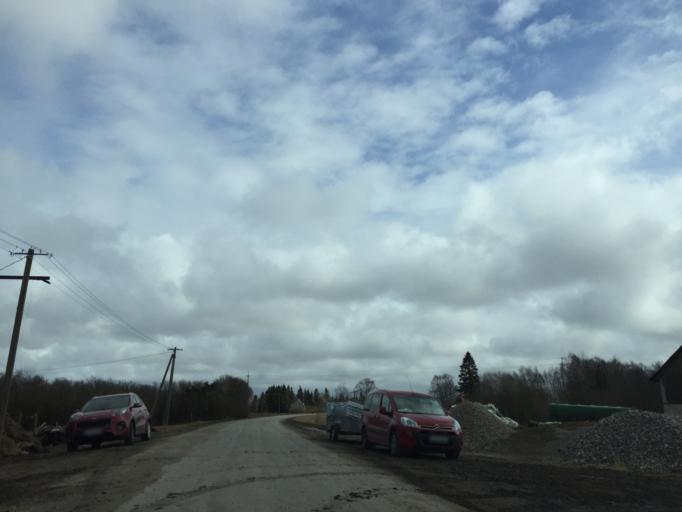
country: EE
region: Laeaene
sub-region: Lihula vald
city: Lihula
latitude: 58.7331
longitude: 23.8656
